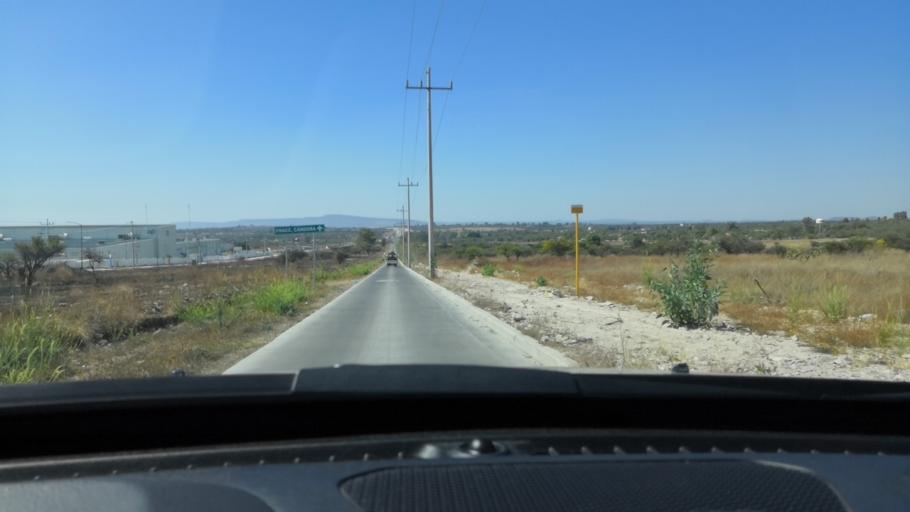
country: MX
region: Guanajuato
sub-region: Leon
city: Centro Familiar la Soledad
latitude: 21.1079
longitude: -101.7632
